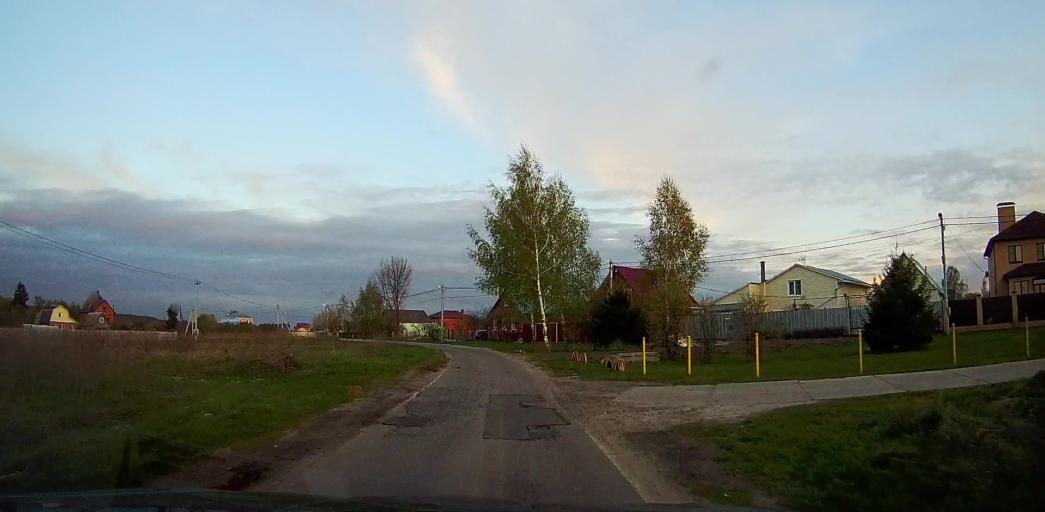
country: RU
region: Moskovskaya
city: Peski
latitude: 55.2123
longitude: 38.7397
